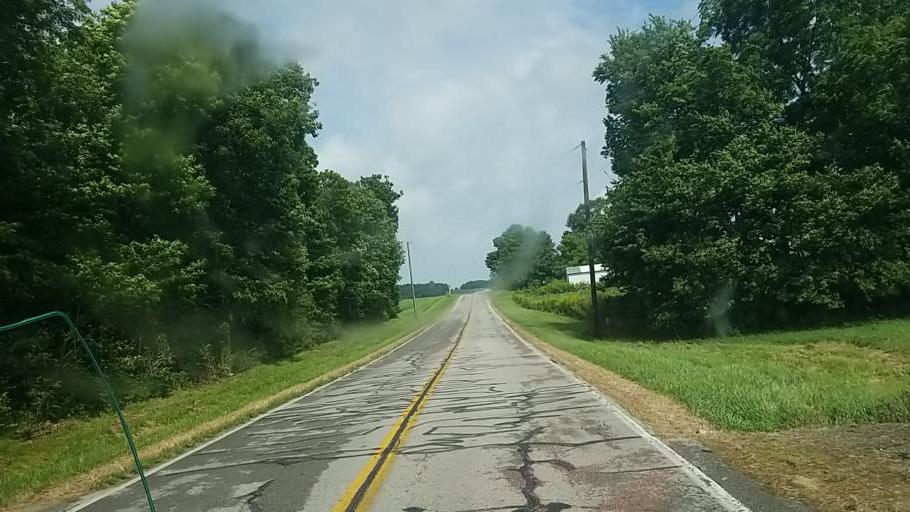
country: US
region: Ohio
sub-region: Logan County
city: West Liberty
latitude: 40.2363
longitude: -83.6724
